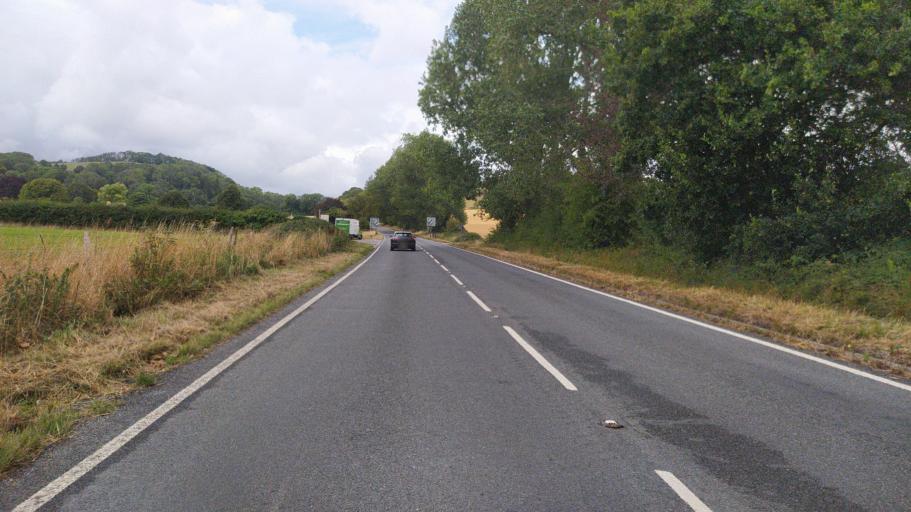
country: GB
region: England
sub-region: Hampshire
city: Petersfield
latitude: 50.9705
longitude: -0.8847
